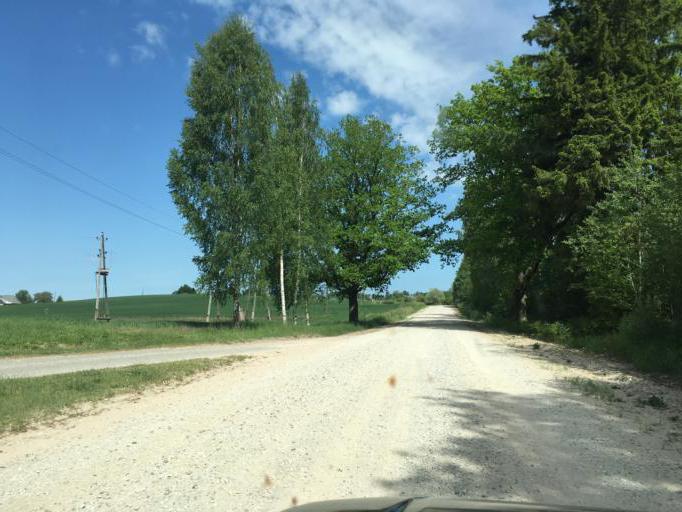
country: LV
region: Talsu Rajons
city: Valdemarpils
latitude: 57.3692
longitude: 22.6214
